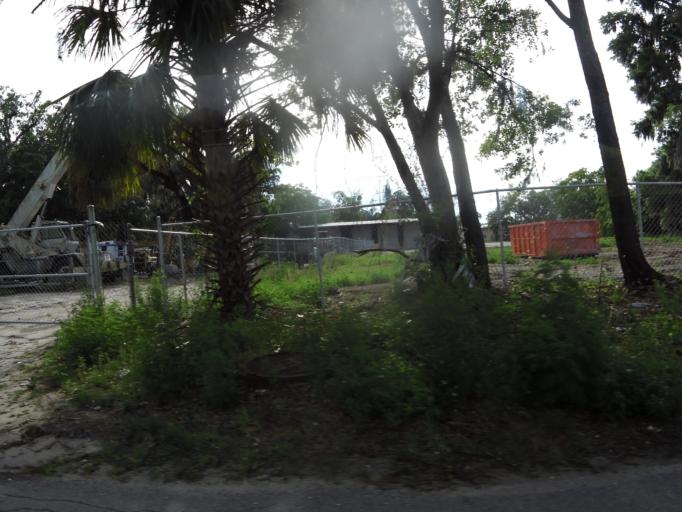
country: US
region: Florida
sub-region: Duval County
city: Jacksonville
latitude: 30.3326
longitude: -81.5978
